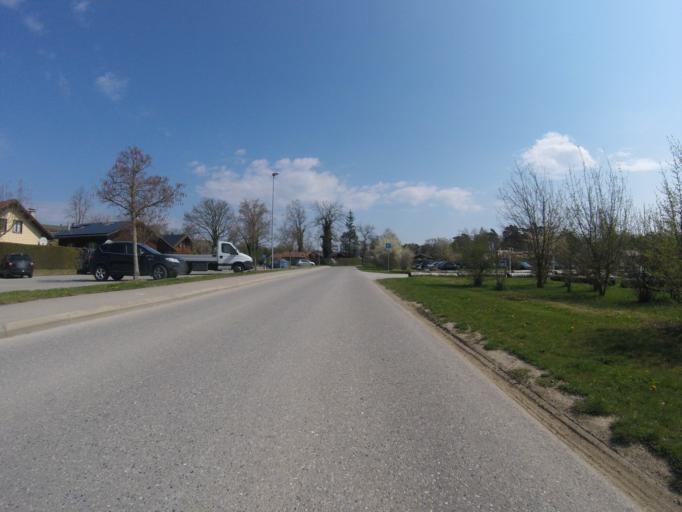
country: CH
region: Vaud
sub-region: Broye-Vully District
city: Avenches
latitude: 46.9152
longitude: 7.0293
